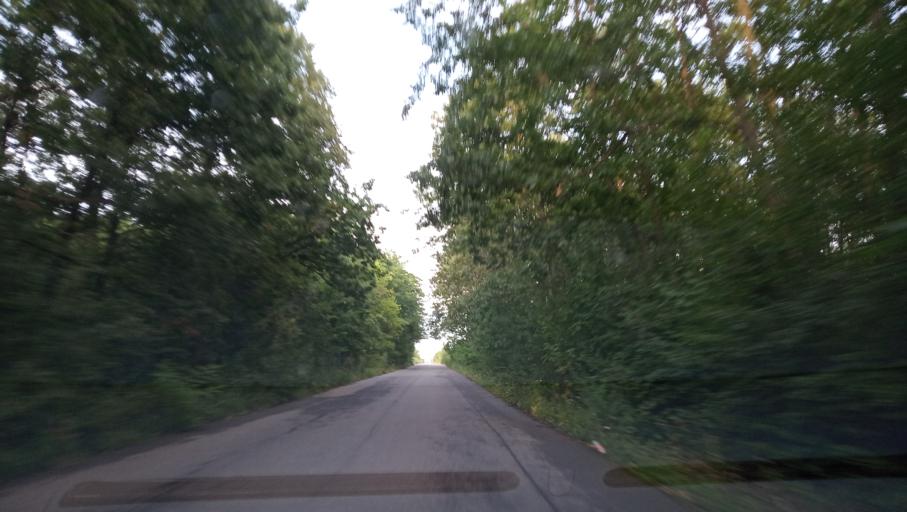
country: RO
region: Giurgiu
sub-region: Comuna Comana
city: Falastoaca
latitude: 44.1732
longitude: 26.1905
